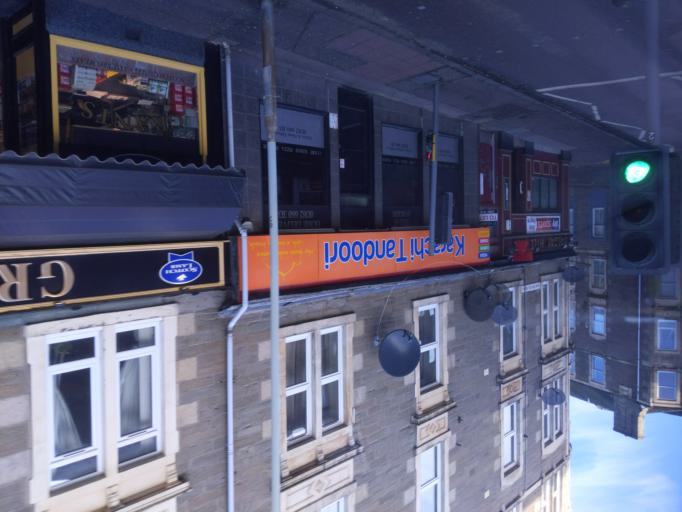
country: GB
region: Scotland
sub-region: Dundee City
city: Dundee
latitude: 56.4603
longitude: -2.9937
